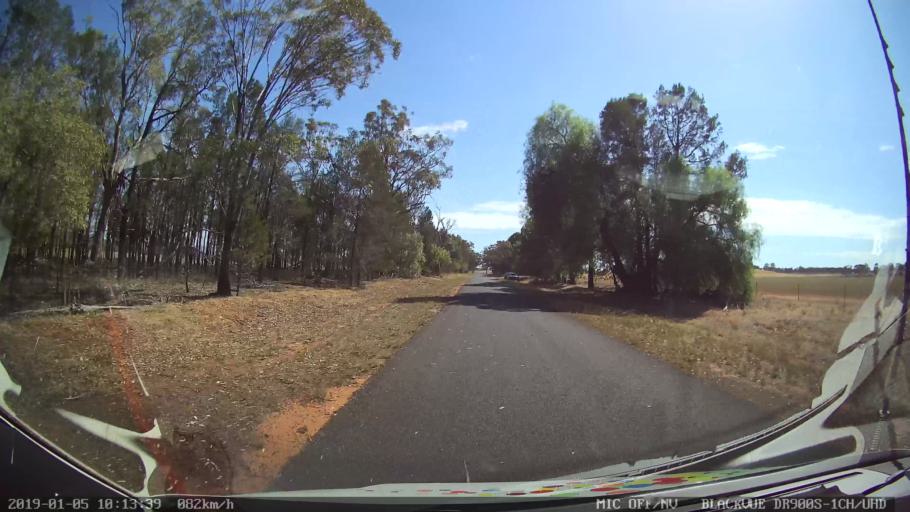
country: AU
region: New South Wales
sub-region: Gilgandra
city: Gilgandra
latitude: -31.6002
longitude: 148.9269
